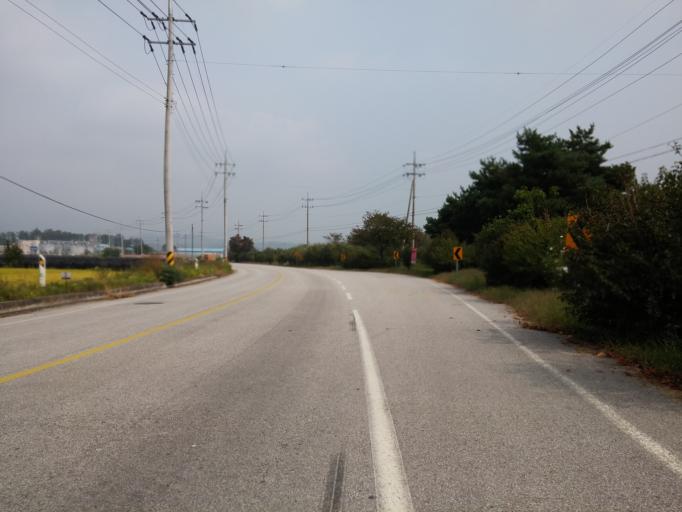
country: KR
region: Chungcheongbuk-do
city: Yong-dong
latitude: 36.4257
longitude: 127.7896
